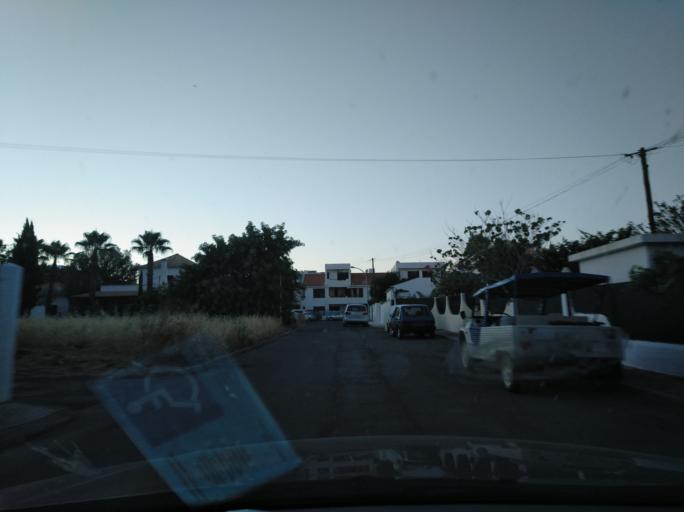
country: PT
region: Faro
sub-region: Tavira
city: Tavira
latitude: 37.1400
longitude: -7.5979
